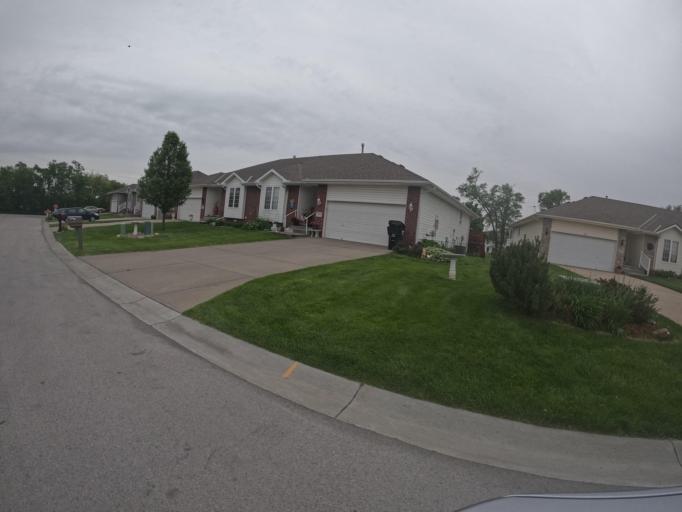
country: US
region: Nebraska
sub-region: Sarpy County
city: Offutt Air Force Base
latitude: 41.0508
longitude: -95.9528
